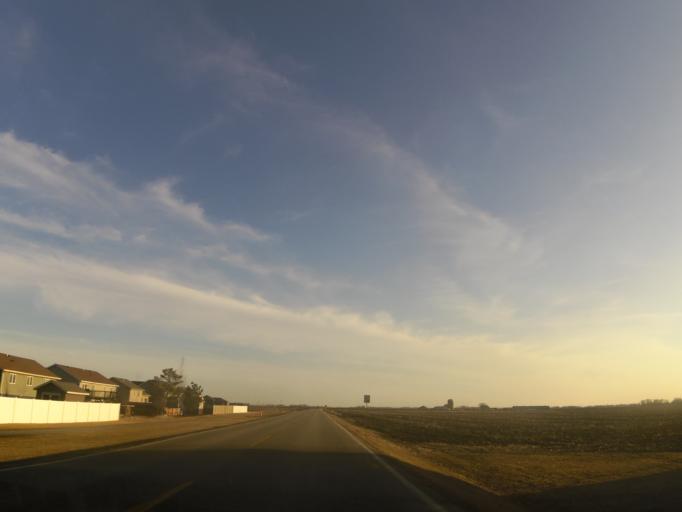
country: US
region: North Dakota
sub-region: Grand Forks County
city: Grand Forks
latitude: 47.8656
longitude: -97.0292
